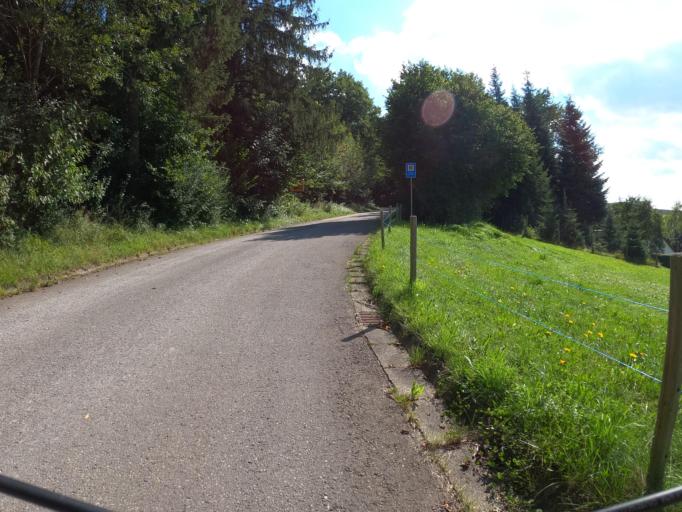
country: DE
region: Bavaria
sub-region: Swabia
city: Roggenburg
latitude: 48.3355
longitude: 10.2226
